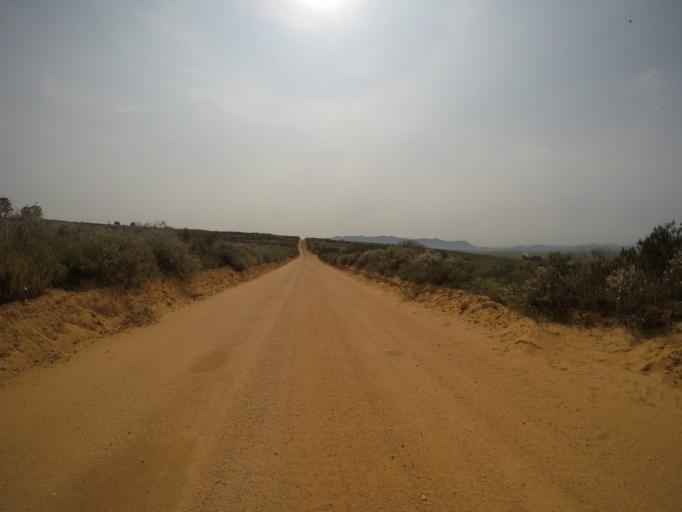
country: ZA
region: Western Cape
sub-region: West Coast District Municipality
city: Malmesbury
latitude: -33.4499
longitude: 18.7456
